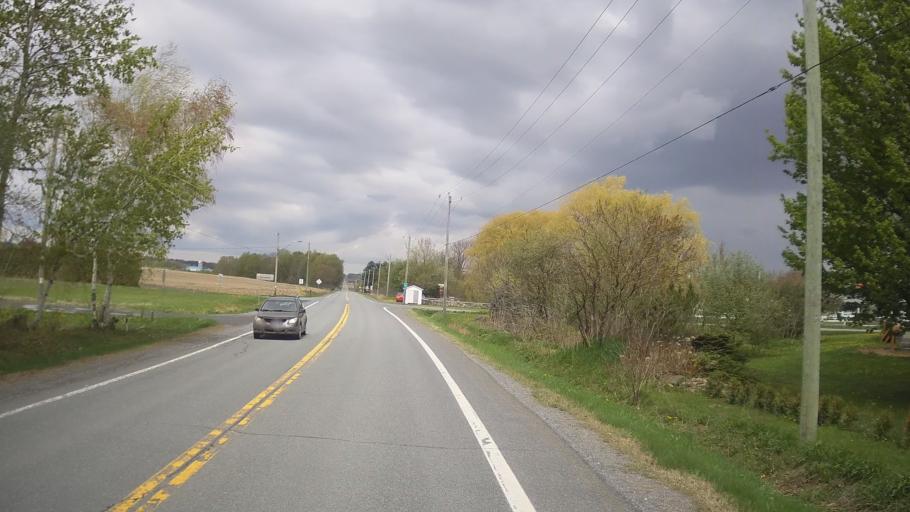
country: CA
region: Quebec
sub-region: Monteregie
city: Farnham
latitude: 45.2458
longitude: -72.8891
